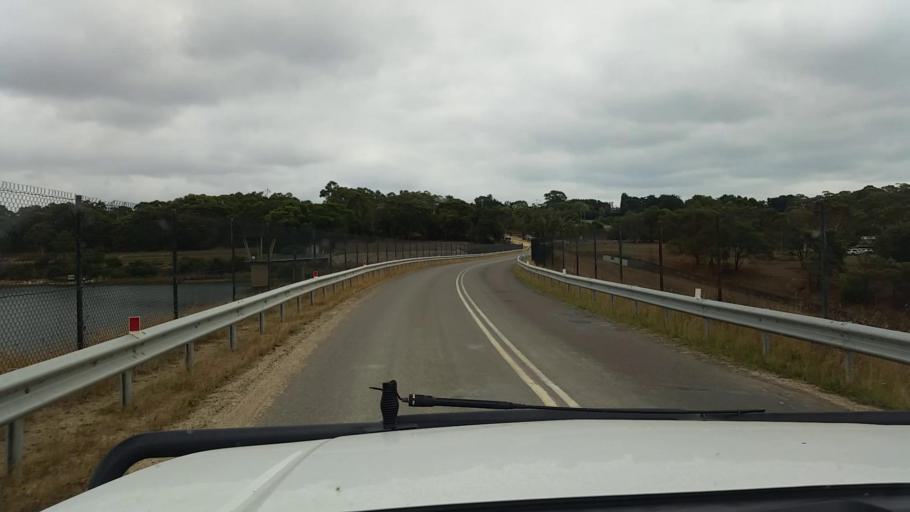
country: AU
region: Victoria
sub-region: Mornington Peninsula
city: Moorooduc
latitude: -38.2781
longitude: 145.1012
